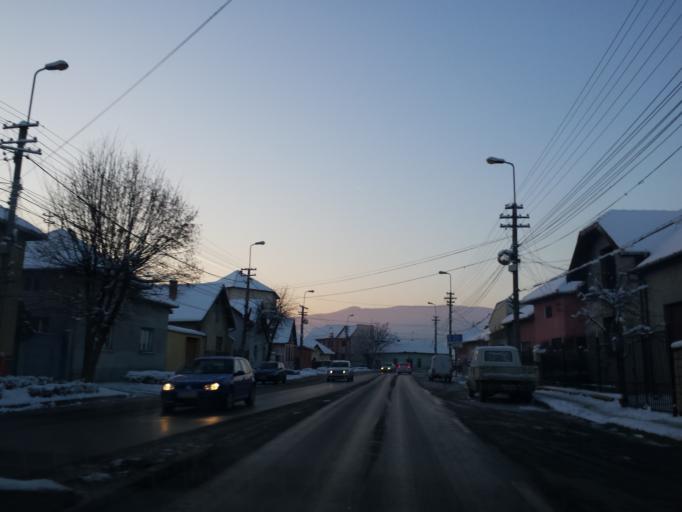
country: RO
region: Alba
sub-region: Municipiul Alba Iulia
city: Alba Iulia
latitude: 46.0736
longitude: 23.5721
